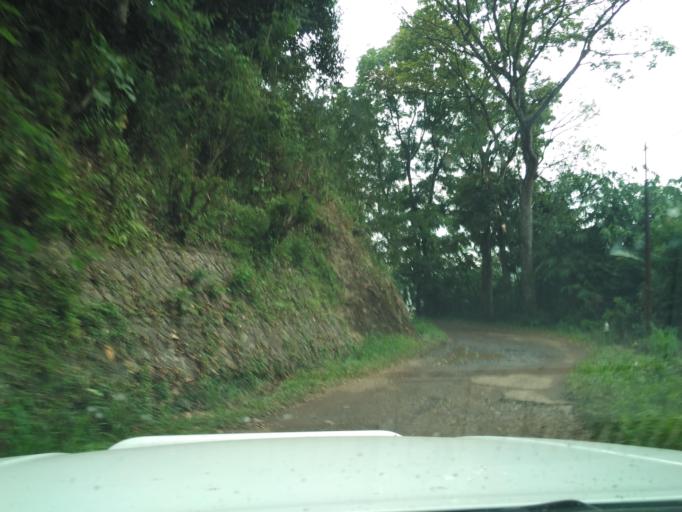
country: ID
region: West Java
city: Ciranjang-hilir
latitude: -6.6962
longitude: 107.1712
